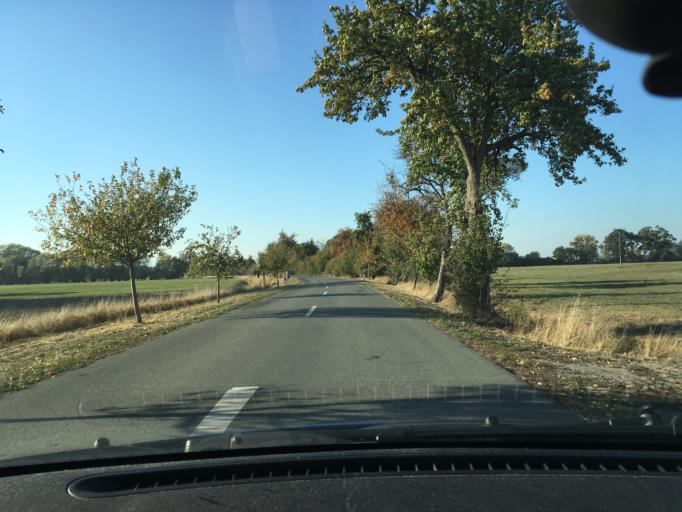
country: DE
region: Lower Saxony
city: Hitzacker
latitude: 53.1515
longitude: 11.0907
